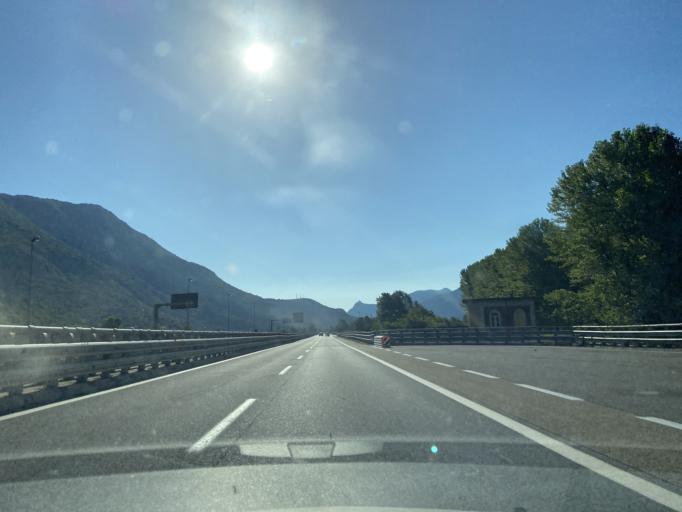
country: IT
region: Piedmont
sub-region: Provincia di Torino
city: San Didero
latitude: 45.1235
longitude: 7.2216
